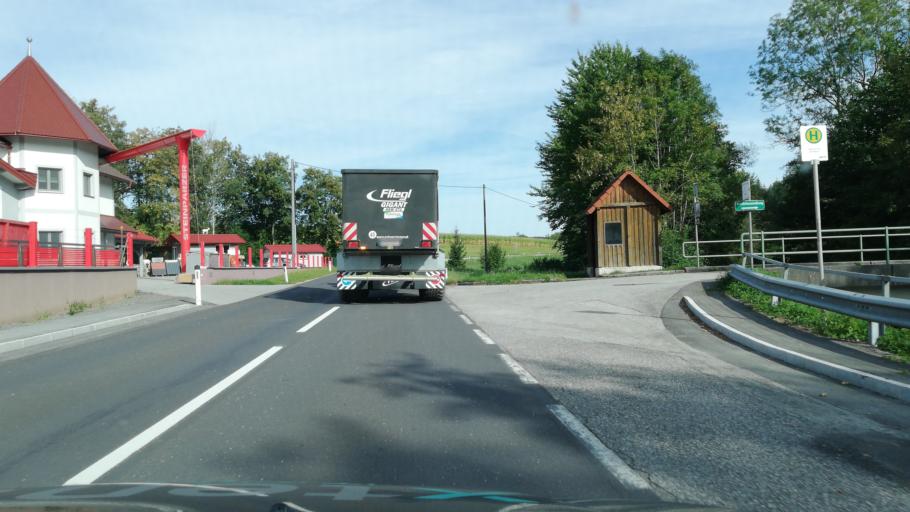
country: AT
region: Lower Austria
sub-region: Politischer Bezirk Amstetten
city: Behamberg
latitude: 48.0272
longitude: 14.4728
